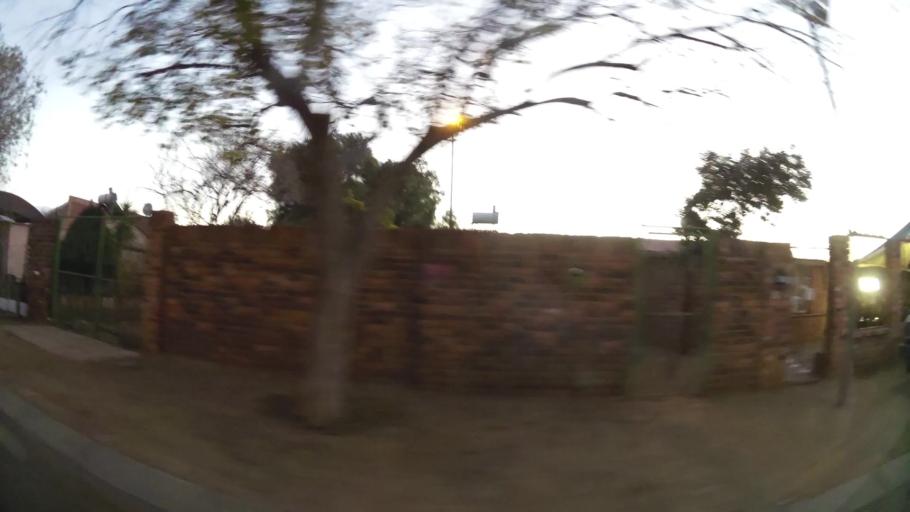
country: ZA
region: Northern Cape
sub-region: Frances Baard District Municipality
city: Kimberley
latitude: -28.7142
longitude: 24.7628
